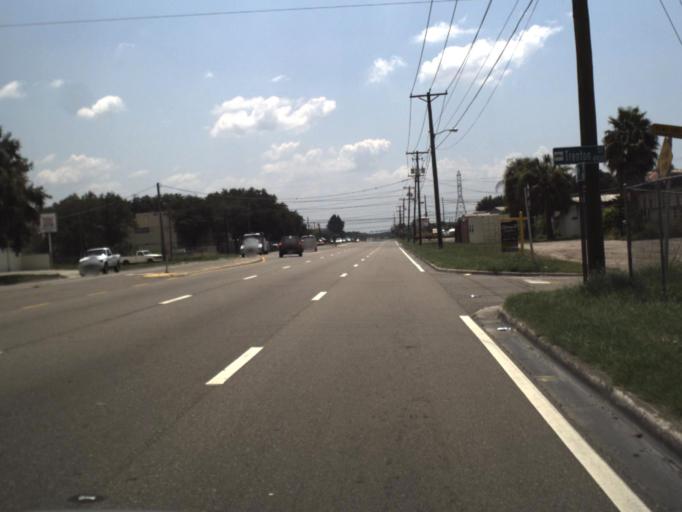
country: US
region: Florida
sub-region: Hillsborough County
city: Palm River-Clair Mel
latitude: 27.9132
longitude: -82.4020
